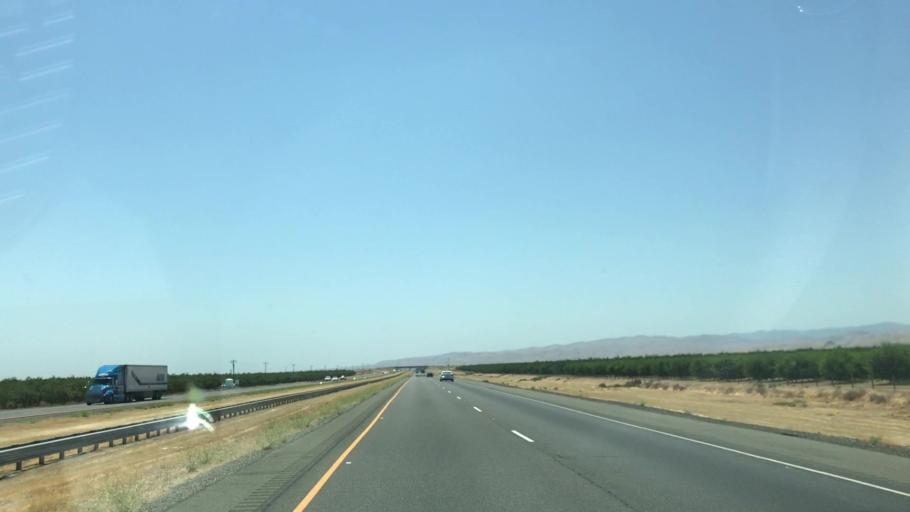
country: US
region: California
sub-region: Merced County
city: South Dos Palos
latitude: 36.7002
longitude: -120.6699
